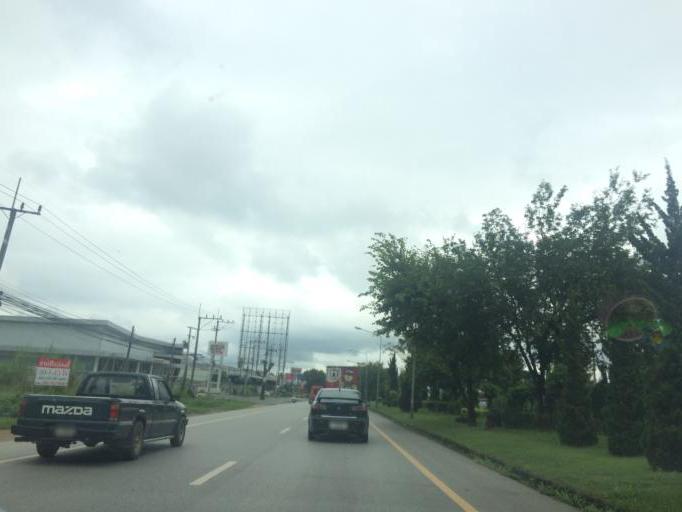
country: TH
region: Chiang Rai
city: Chiang Rai
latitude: 19.8649
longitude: 99.8227
